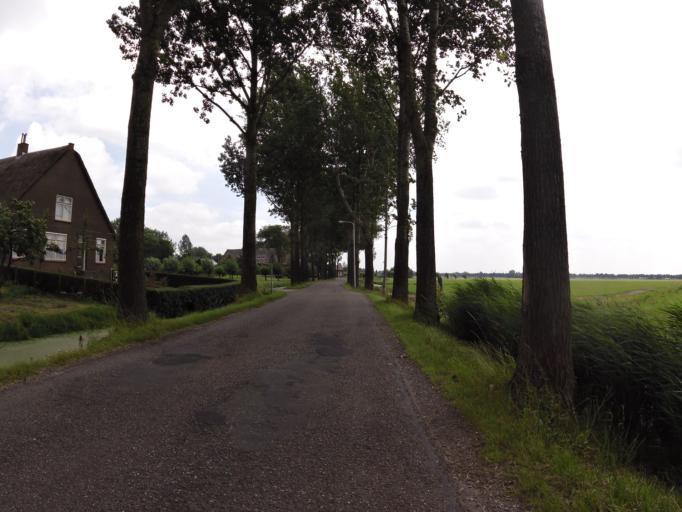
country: NL
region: South Holland
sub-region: Gemeente Leerdam
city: Leerdam
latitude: 51.9057
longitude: 5.0562
